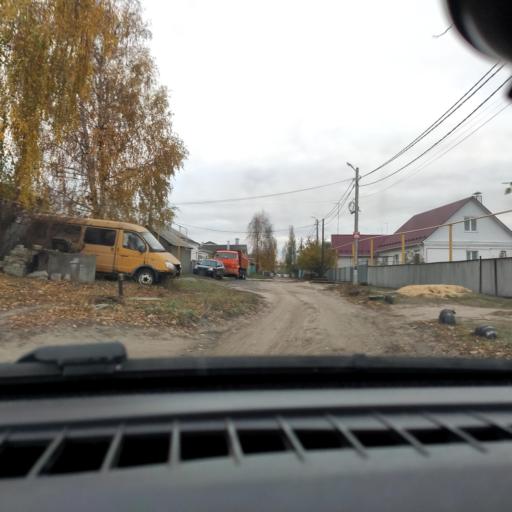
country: RU
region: Voronezj
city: Podgornoye
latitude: 51.7344
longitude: 39.1423
